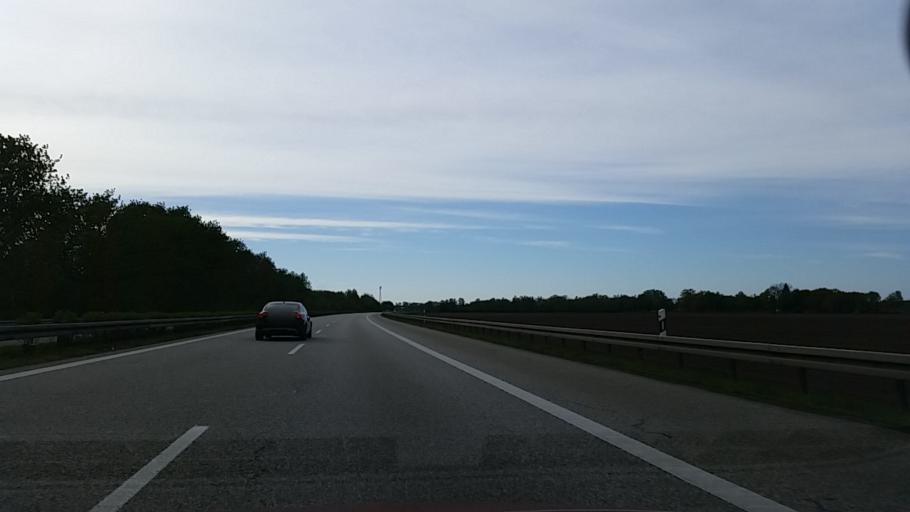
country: DE
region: Mecklenburg-Vorpommern
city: Neustadt-Glewe
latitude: 53.3979
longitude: 11.5842
